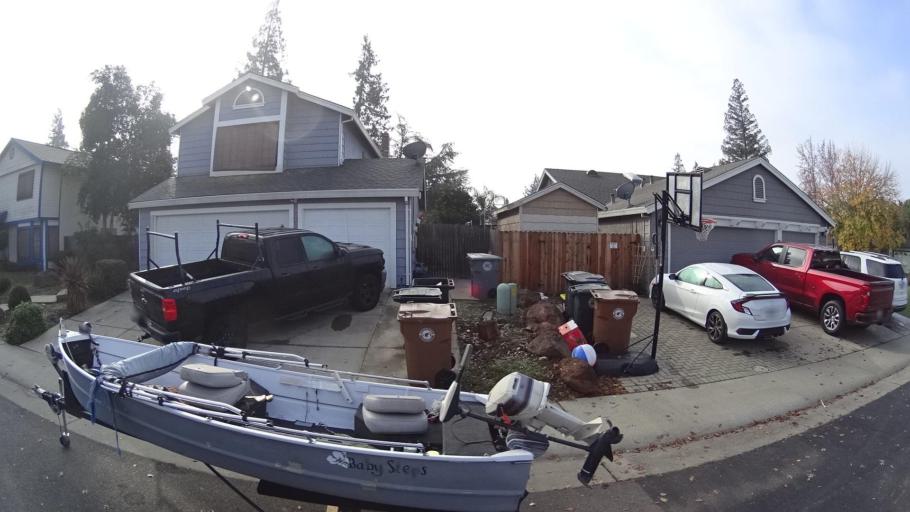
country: US
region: California
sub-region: Sacramento County
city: Elk Grove
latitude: 38.3993
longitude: -121.3639
